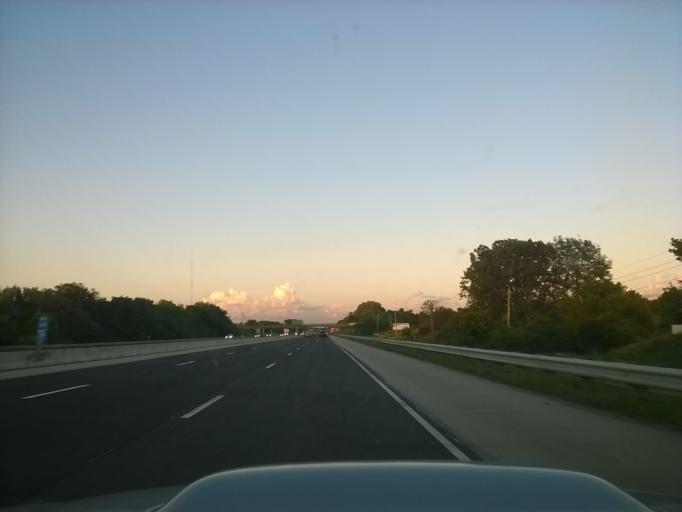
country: US
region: Indiana
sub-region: Marion County
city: Meridian Hills
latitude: 39.9240
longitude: -86.2068
